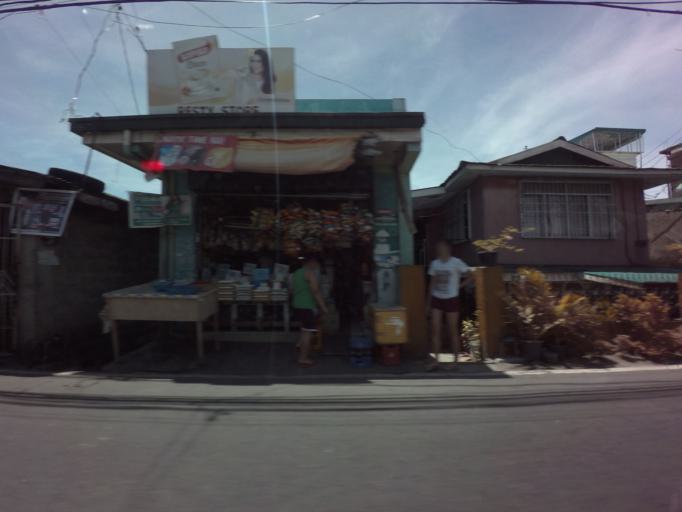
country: PH
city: Sambayanihan People's Village
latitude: 14.4552
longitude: 121.0527
